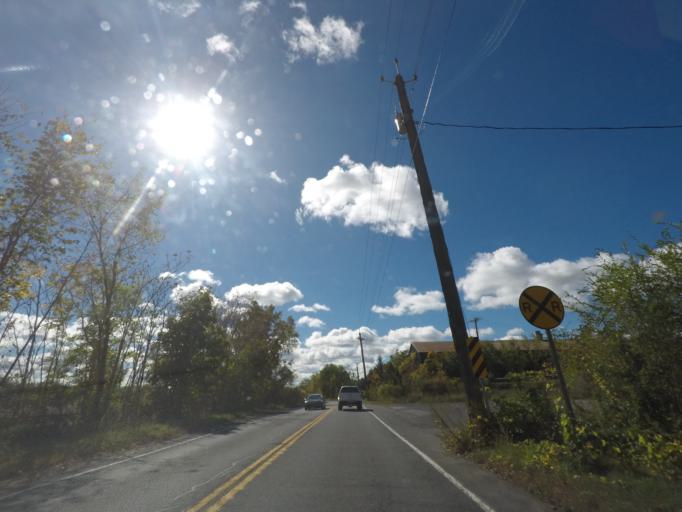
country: US
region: New York
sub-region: Albany County
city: Menands
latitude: 42.7121
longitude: -73.7199
